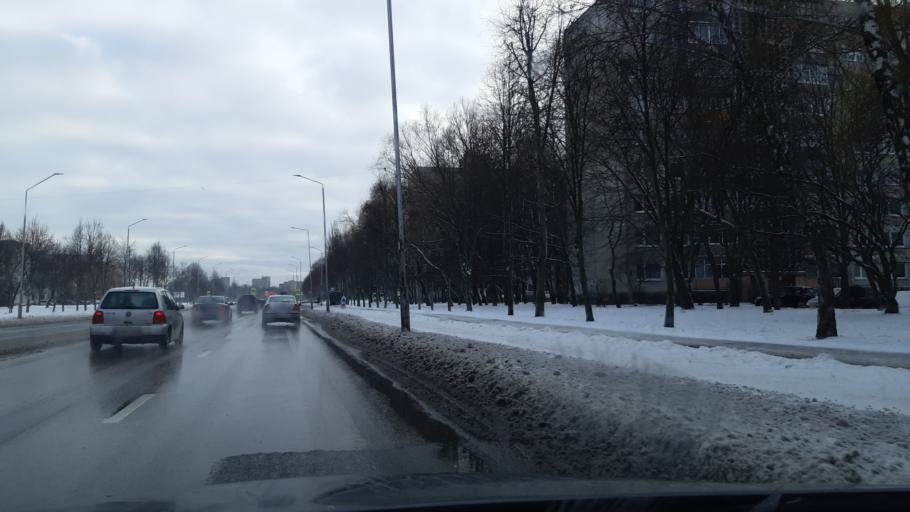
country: LT
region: Kauno apskritis
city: Dainava (Kaunas)
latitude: 54.9261
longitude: 23.9750
